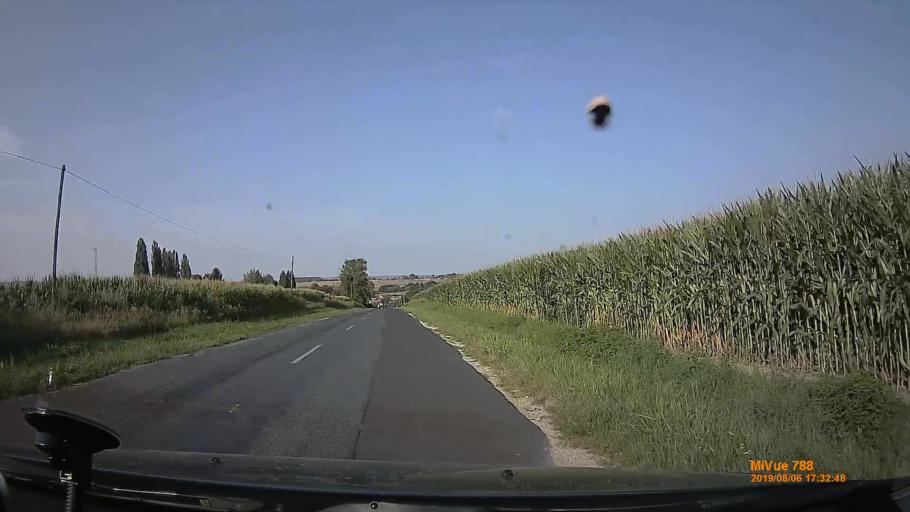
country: HU
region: Zala
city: Murakeresztur
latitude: 46.4265
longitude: 16.8851
